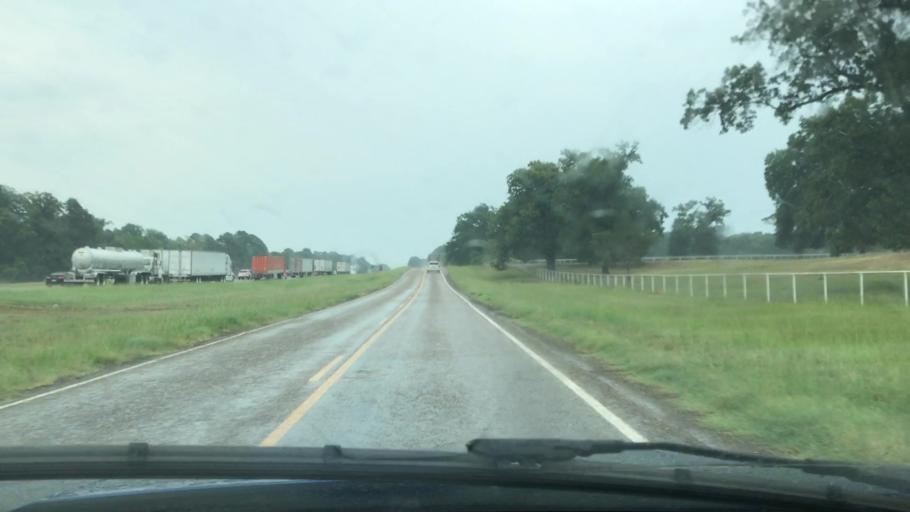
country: US
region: Texas
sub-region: Harrison County
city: Waskom
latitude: 32.4869
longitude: -94.1312
